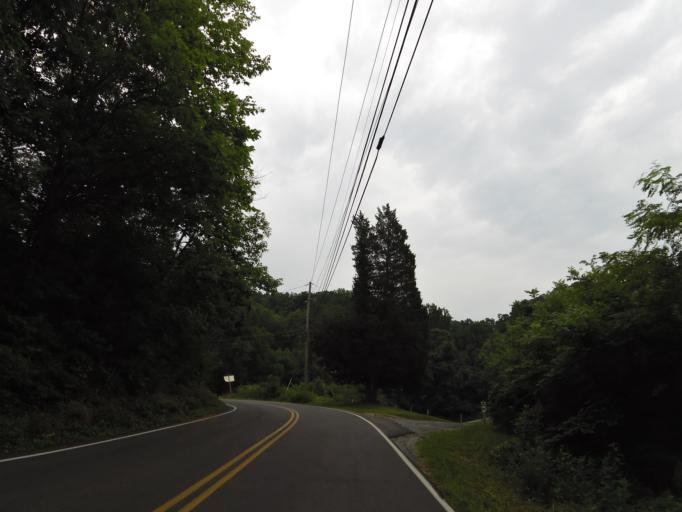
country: US
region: Tennessee
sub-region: Knox County
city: Knoxville
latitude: 35.9208
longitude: -83.8507
